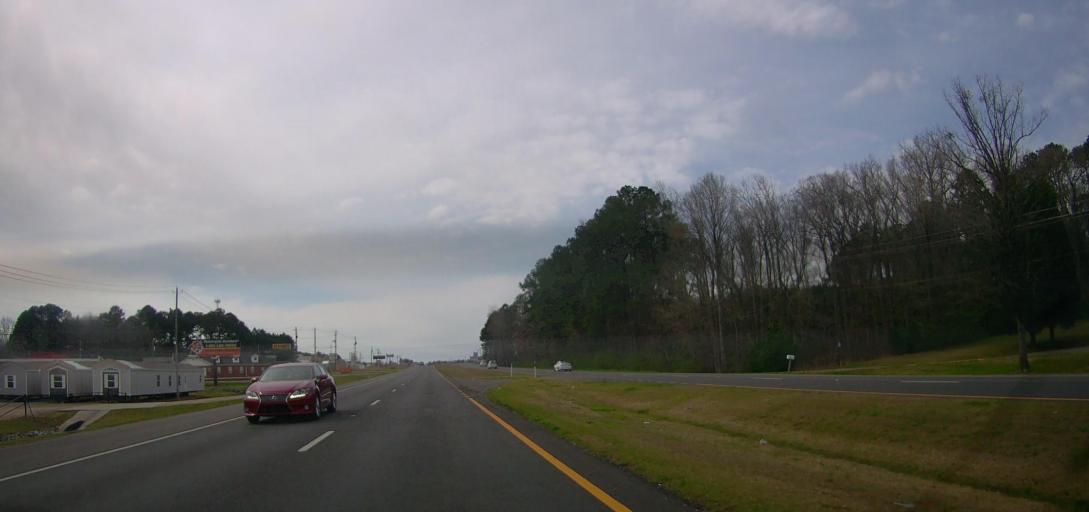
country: US
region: Alabama
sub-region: Walker County
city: Jasper
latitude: 33.8346
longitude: -87.2202
